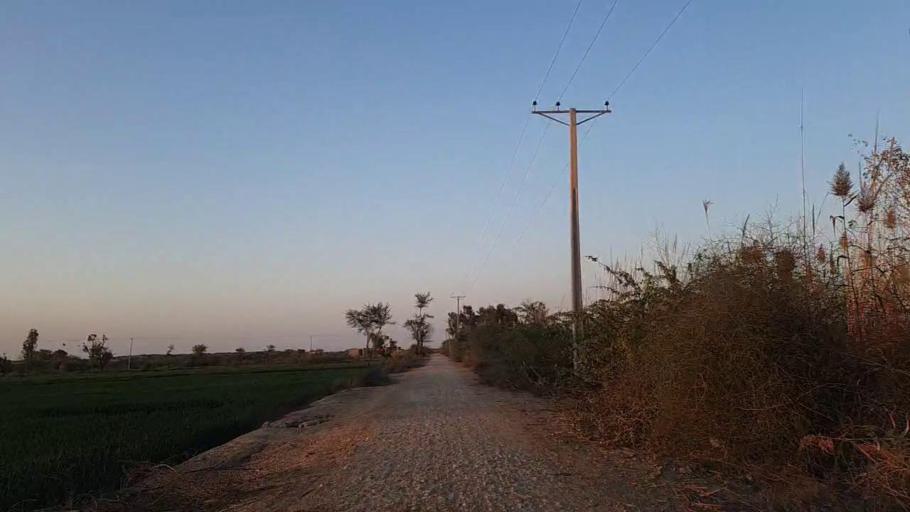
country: PK
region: Sindh
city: Jam Sahib
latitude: 26.3119
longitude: 68.6536
